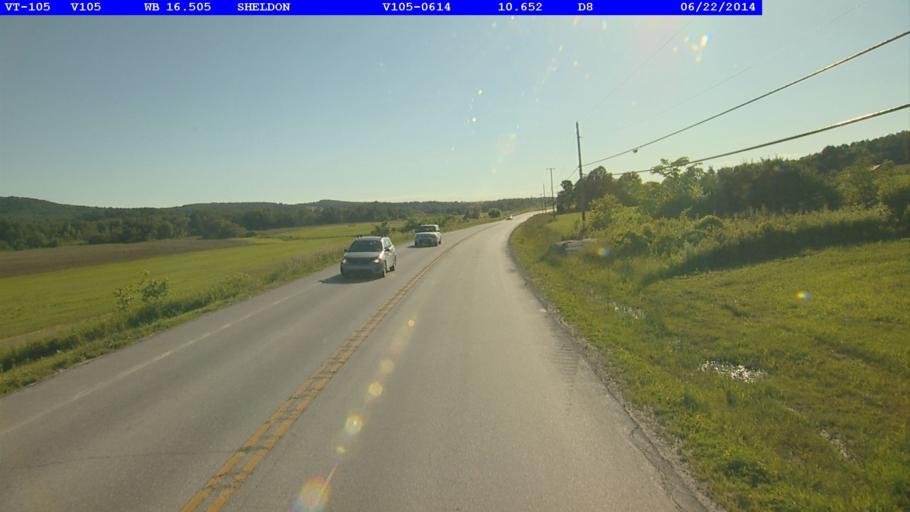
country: US
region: Vermont
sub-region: Franklin County
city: Enosburg Falls
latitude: 44.9073
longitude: -72.8270
